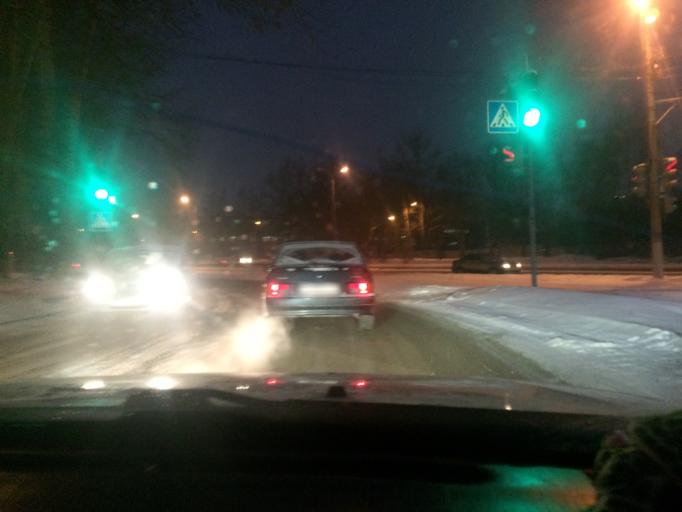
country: RU
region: Tula
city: Mendeleyevskiy
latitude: 54.1555
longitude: 37.5928
